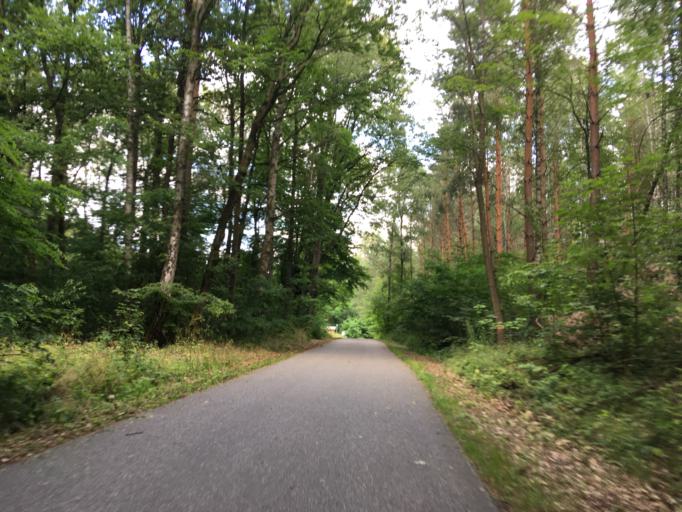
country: DE
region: Brandenburg
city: Bernau bei Berlin
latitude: 52.6914
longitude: 13.5402
